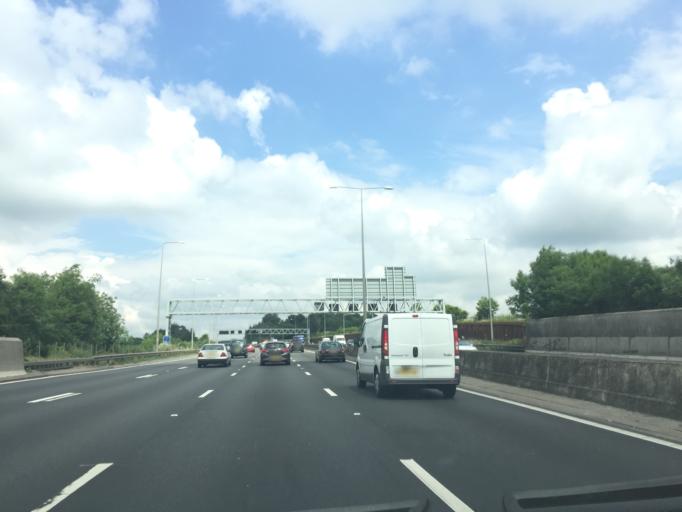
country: GB
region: England
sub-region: Hertfordshire
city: Kings Langley
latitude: 51.7052
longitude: -0.4374
